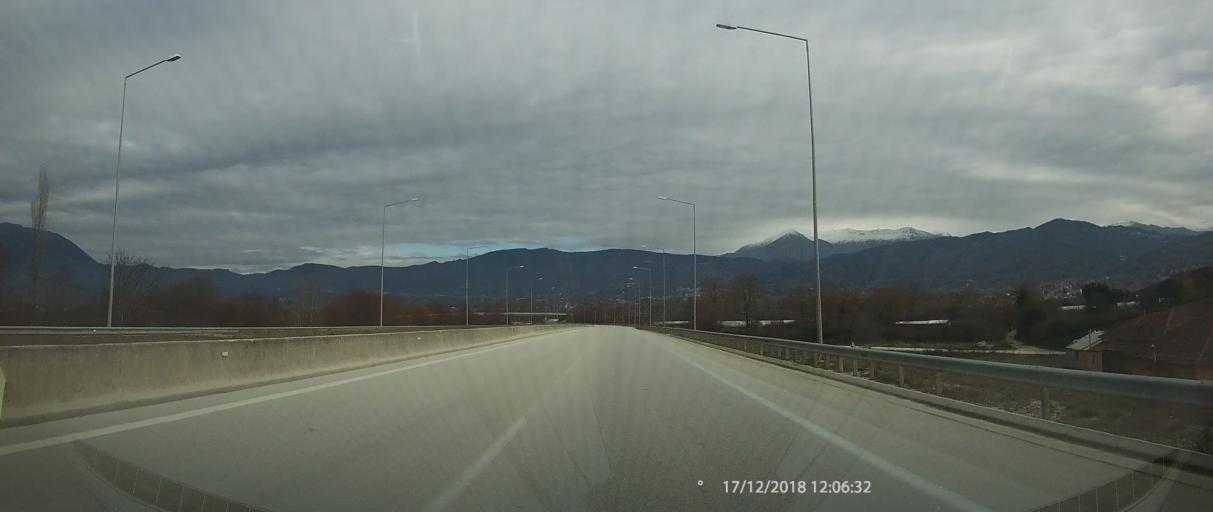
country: GR
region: Epirus
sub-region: Nomos Ioanninon
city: Koutselio
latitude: 39.6081
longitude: 20.9374
